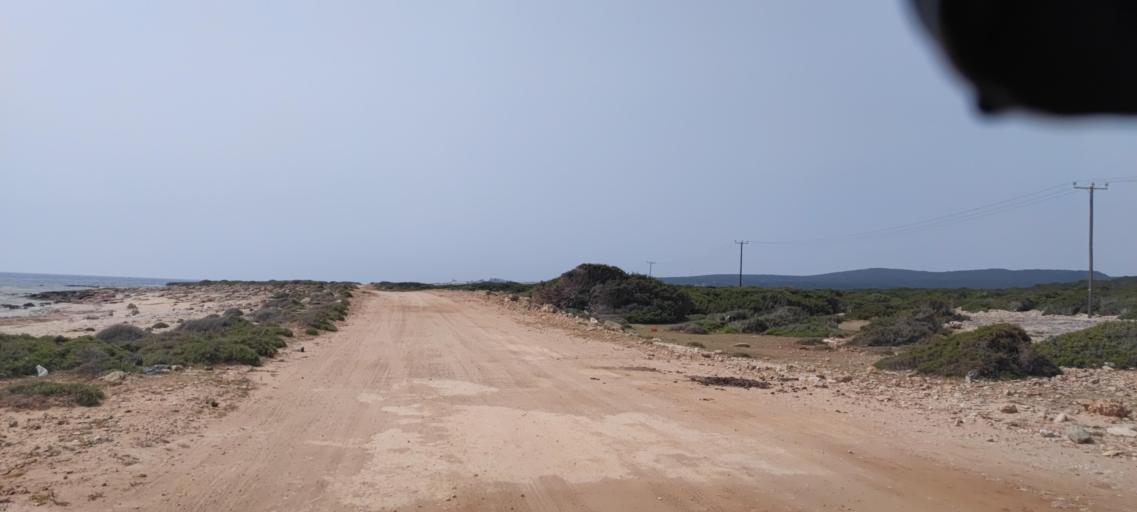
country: CY
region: Ammochostos
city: Rizokarpaso
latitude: 35.6765
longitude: 34.5778
